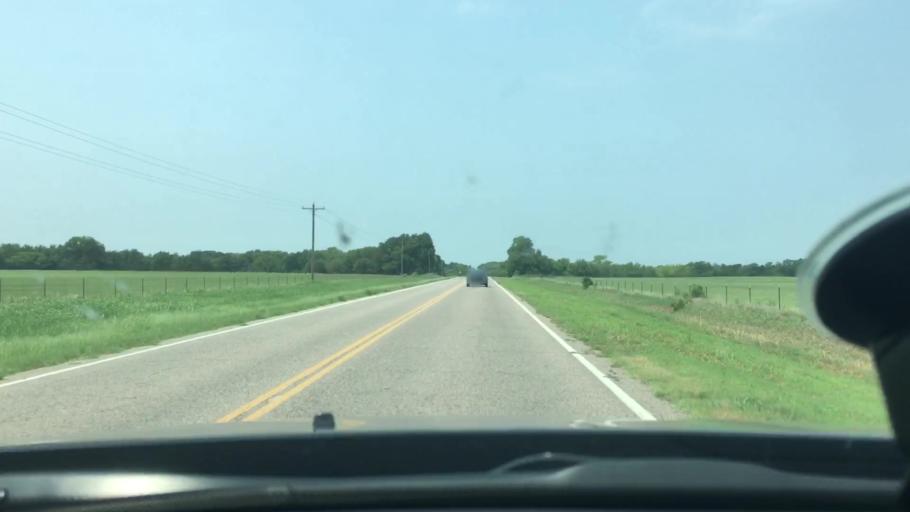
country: US
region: Texas
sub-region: Grayson County
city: Sherwood Shores
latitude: 33.9840
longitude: -96.9279
